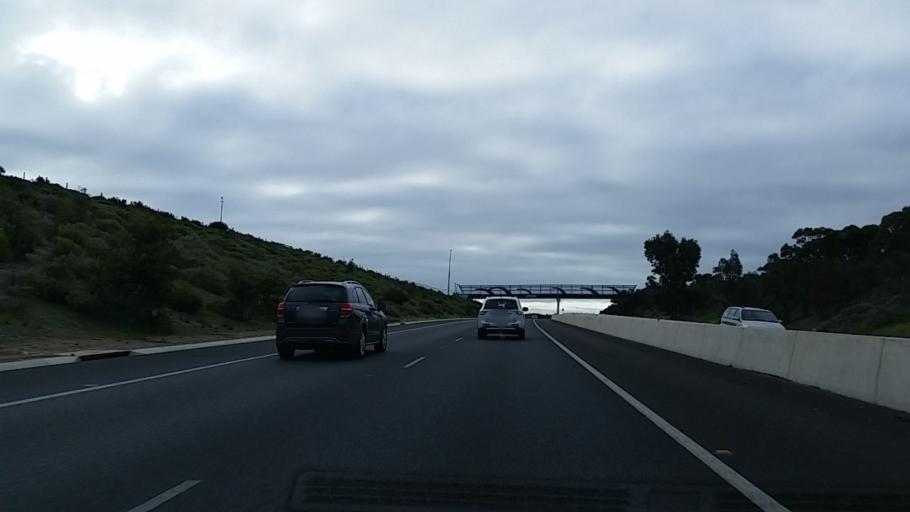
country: AU
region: South Australia
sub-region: Onkaparinga
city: Noarlunga Downs
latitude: -35.1596
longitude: 138.5067
